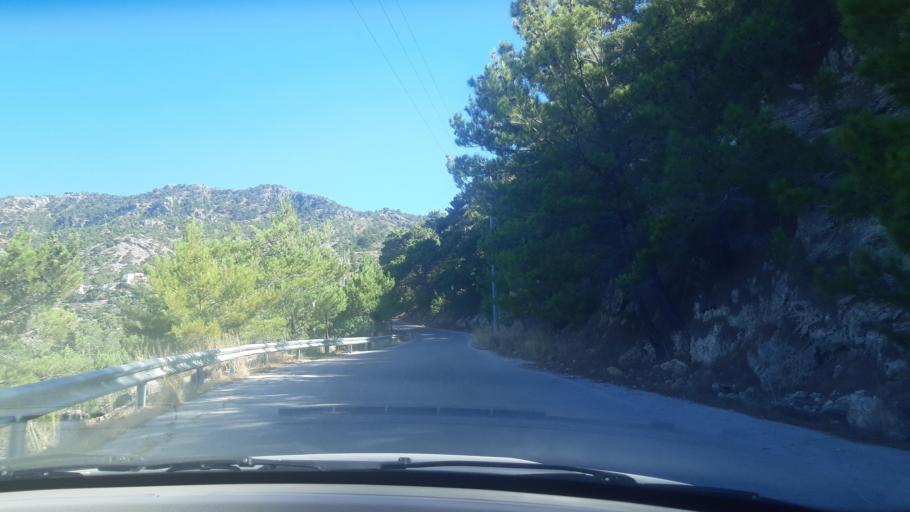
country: GR
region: South Aegean
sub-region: Nomos Dodekanisou
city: Karpathos
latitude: 35.5815
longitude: 27.1790
